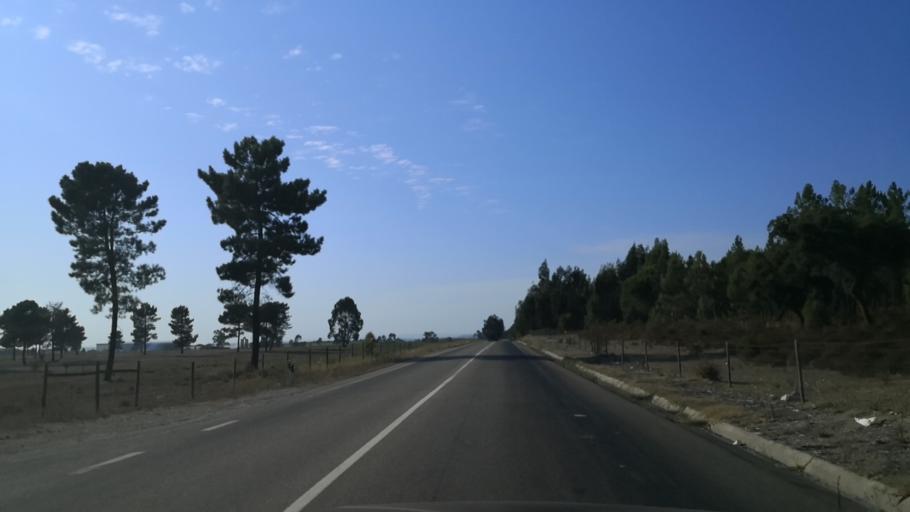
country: PT
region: Santarem
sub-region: Almeirim
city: Fazendas de Almeirim
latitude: 39.1193
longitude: -8.5984
